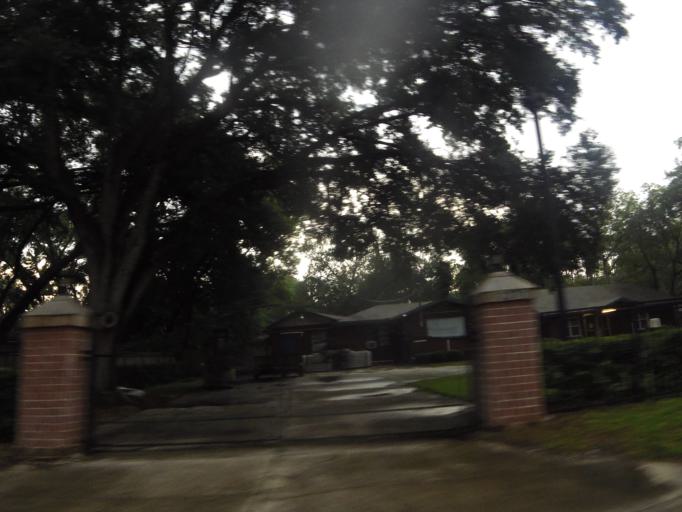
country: US
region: Florida
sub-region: Duval County
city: Jacksonville
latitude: 30.2662
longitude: -81.5816
